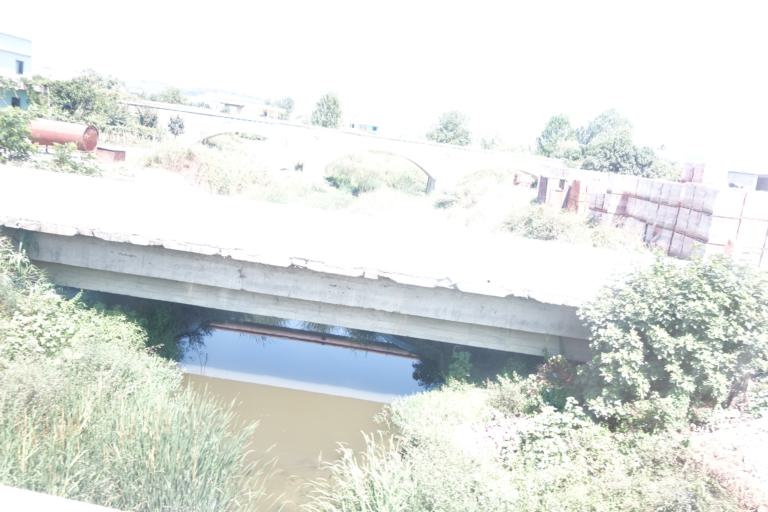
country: AL
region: Tirane
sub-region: Rrethi i Tiranes
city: Shengjergj
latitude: 41.2048
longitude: 19.5351
